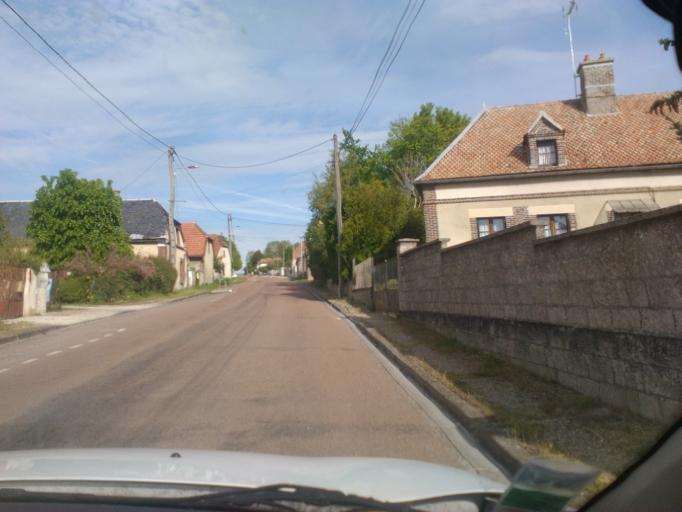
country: FR
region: Champagne-Ardenne
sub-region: Departement de l'Aube
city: Payns
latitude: 48.3706
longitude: 3.8968
